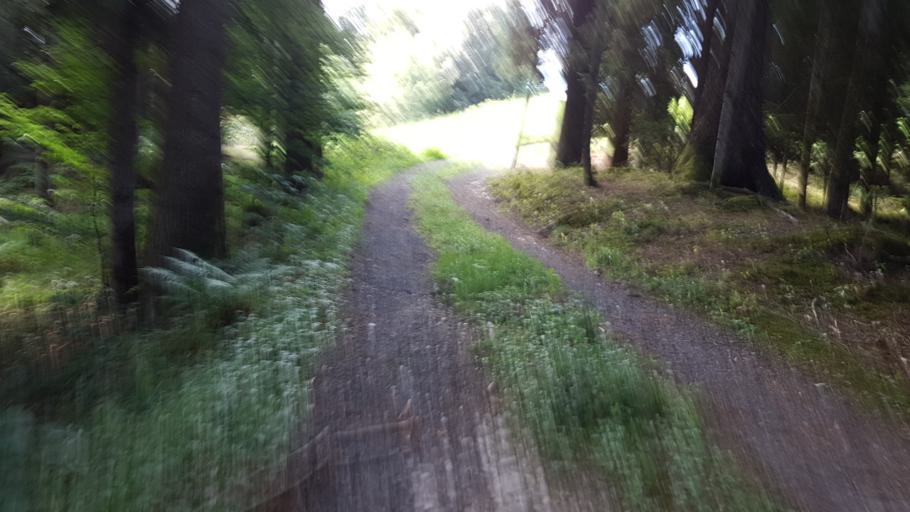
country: CH
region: Bern
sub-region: Bern-Mittelland District
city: Linden
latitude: 46.8446
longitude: 7.7182
